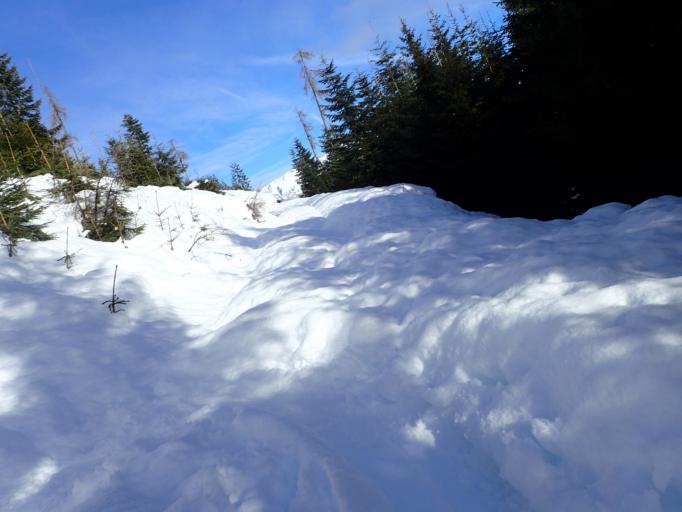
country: AT
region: Salzburg
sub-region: Politischer Bezirk Sankt Johann im Pongau
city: Bischofshofen
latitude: 47.4047
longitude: 13.1686
